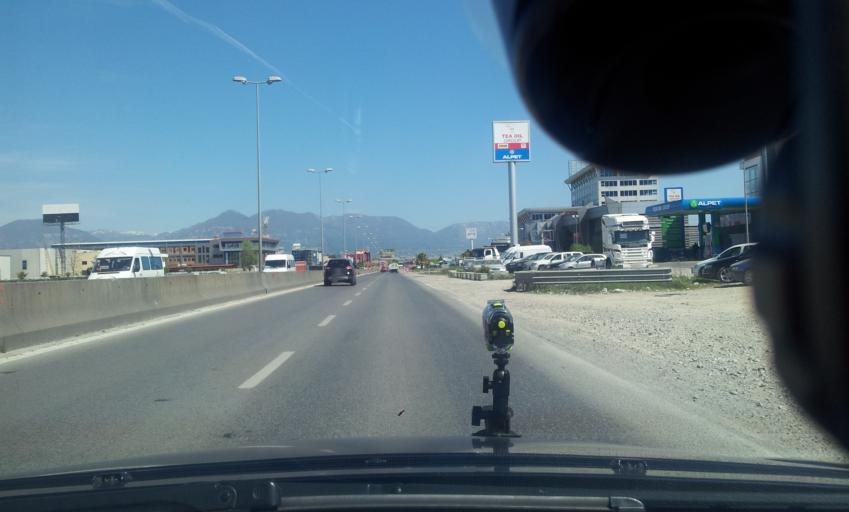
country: AL
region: Tirane
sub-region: Rrethi i Tiranes
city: Berxull
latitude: 41.3688
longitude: 19.6932
